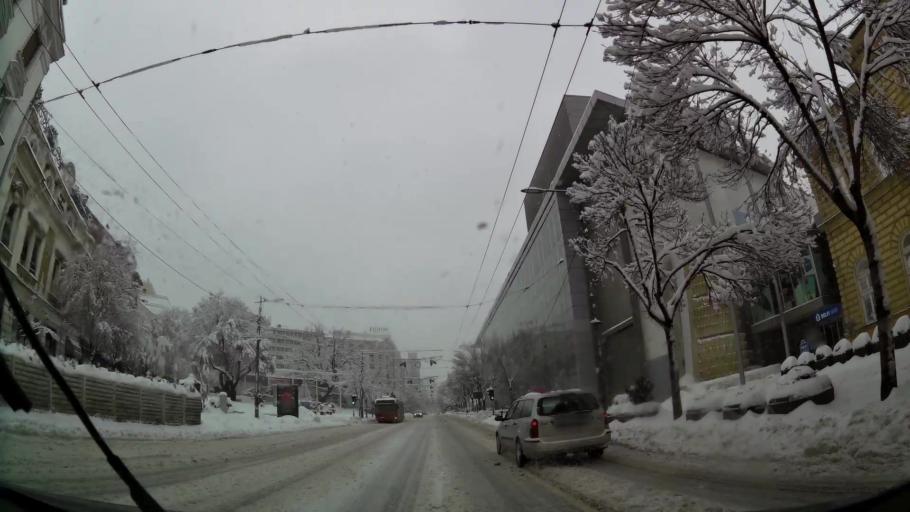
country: RS
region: Central Serbia
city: Belgrade
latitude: 44.8062
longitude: 20.4646
